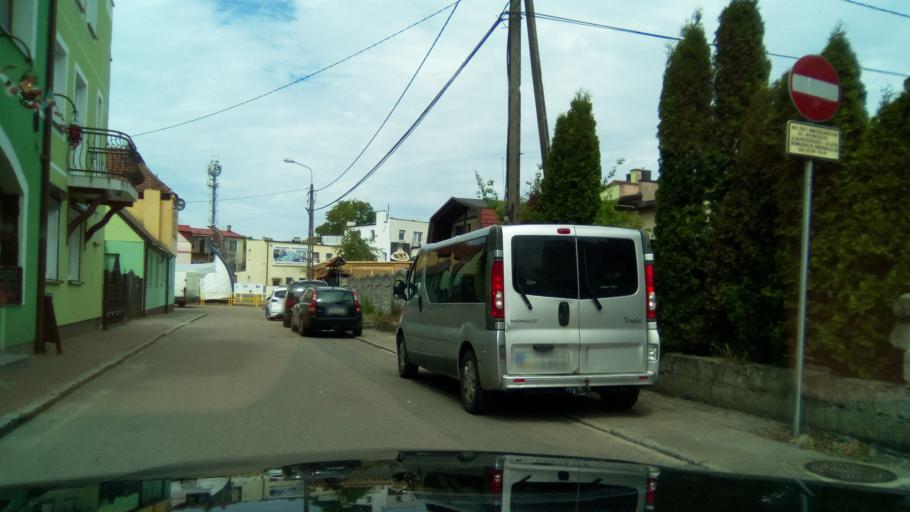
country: PL
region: Pomeranian Voivodeship
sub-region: Powiat leborski
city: Leba
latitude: 54.7593
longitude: 17.5540
